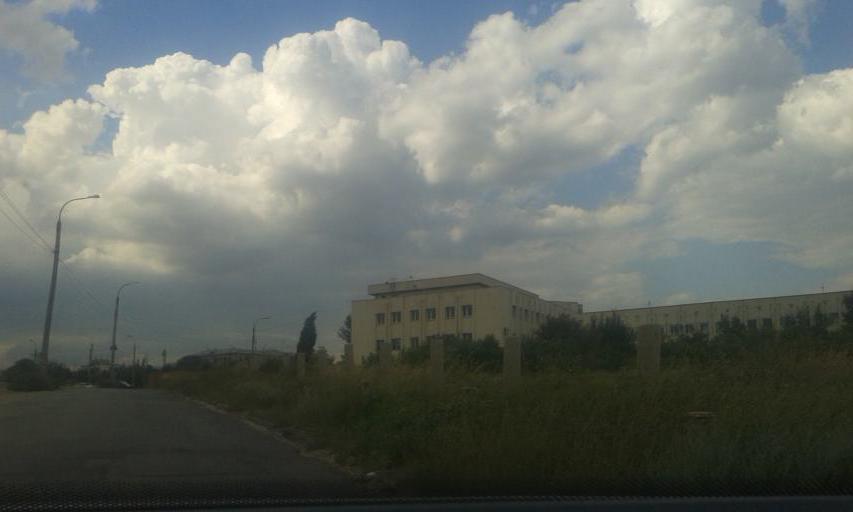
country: RU
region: Volgograd
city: Volgograd
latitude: 48.6398
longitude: 44.4218
